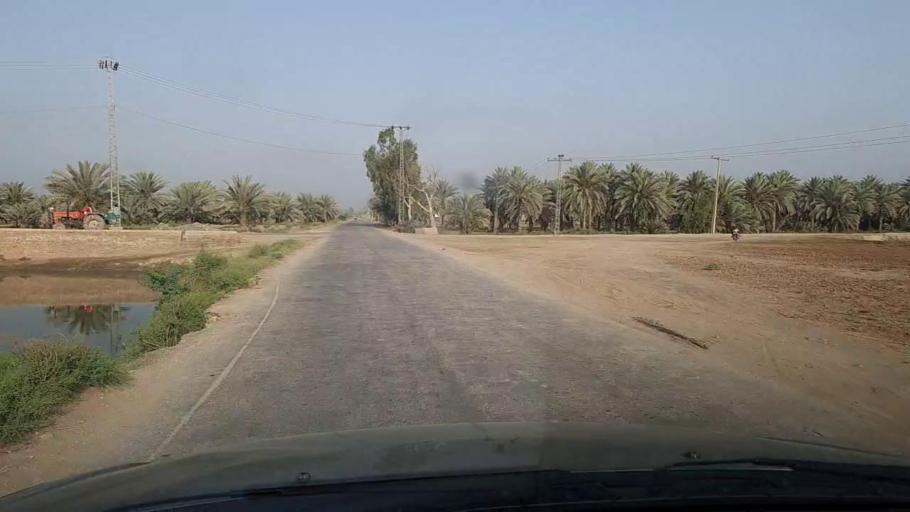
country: PK
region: Sindh
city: Pir jo Goth
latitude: 27.5685
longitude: 68.6382
